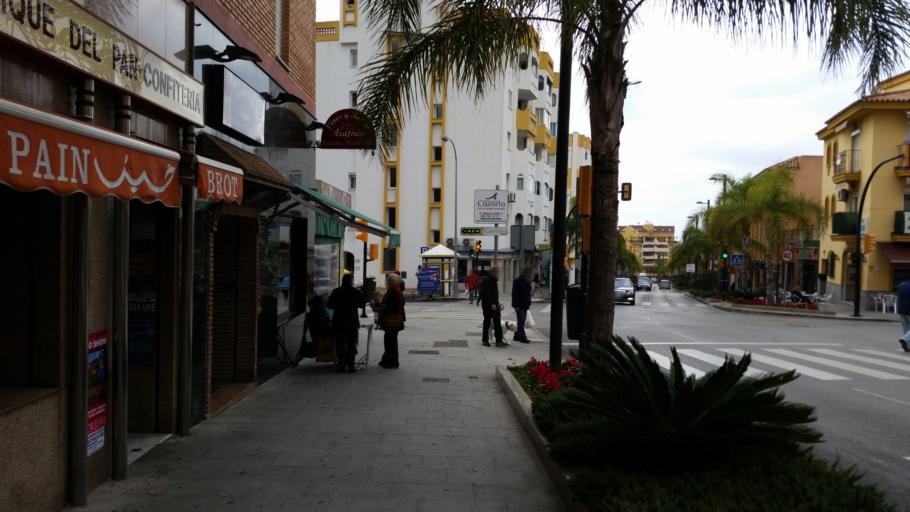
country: ES
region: Andalusia
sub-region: Provincia de Malaga
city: Benalmadena
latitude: 36.5986
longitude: -4.5315
